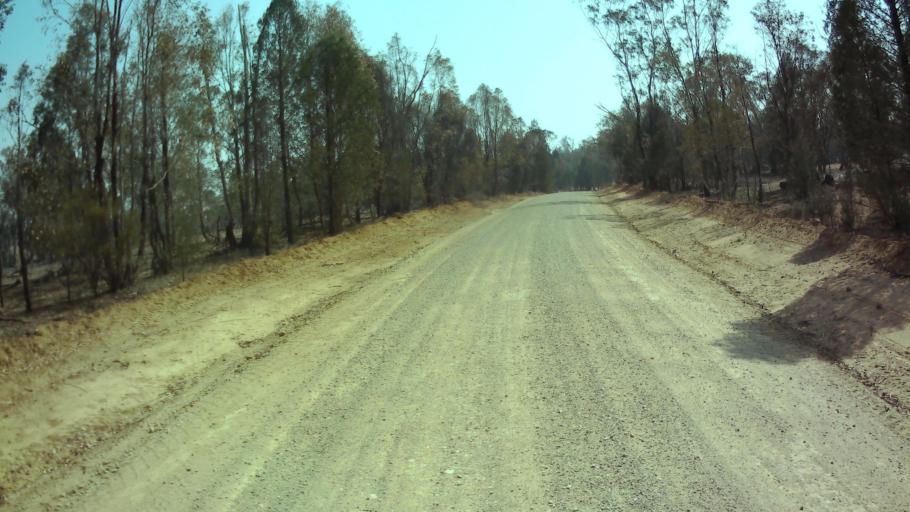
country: AU
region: New South Wales
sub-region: Weddin
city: Grenfell
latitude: -33.6634
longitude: 148.2743
